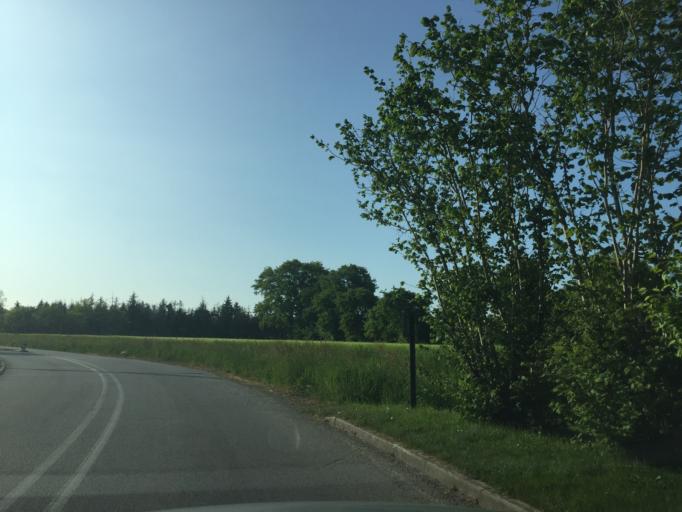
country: FR
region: Brittany
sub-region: Departement des Cotes-d'Armor
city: Crehen
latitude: 48.5508
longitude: -2.2331
